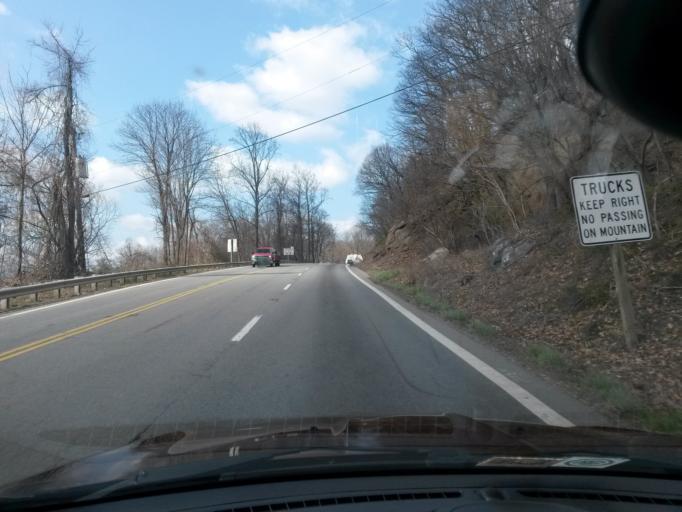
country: US
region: Virginia
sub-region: City of Waynesboro
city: Waynesboro
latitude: 38.0376
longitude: -78.8378
